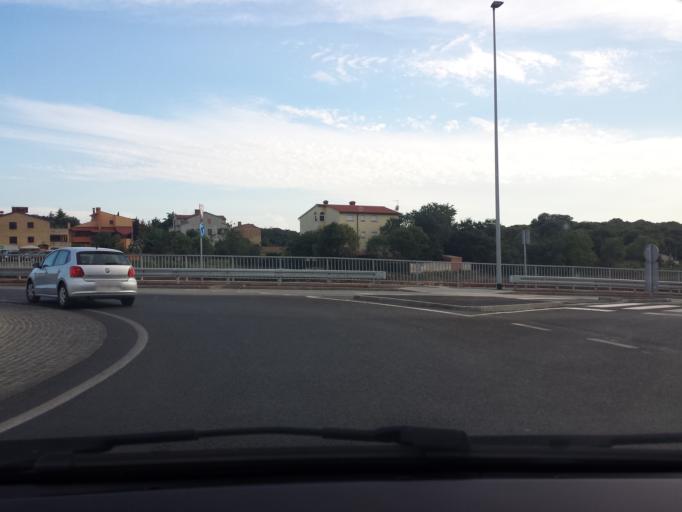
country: HR
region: Istarska
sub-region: Grad Pula
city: Pula
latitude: 44.8991
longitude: 13.8449
